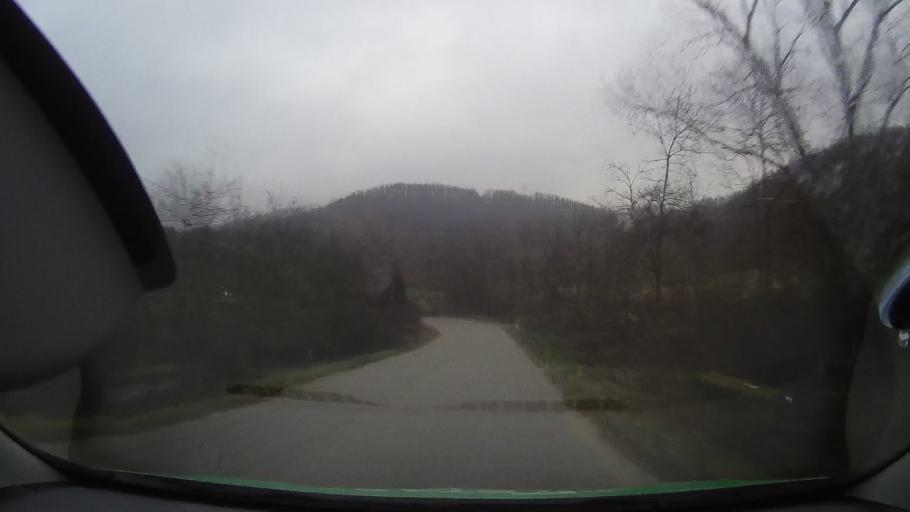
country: RO
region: Hunedoara
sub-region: Comuna Ribita
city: Ribita
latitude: 46.2335
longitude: 22.7463
